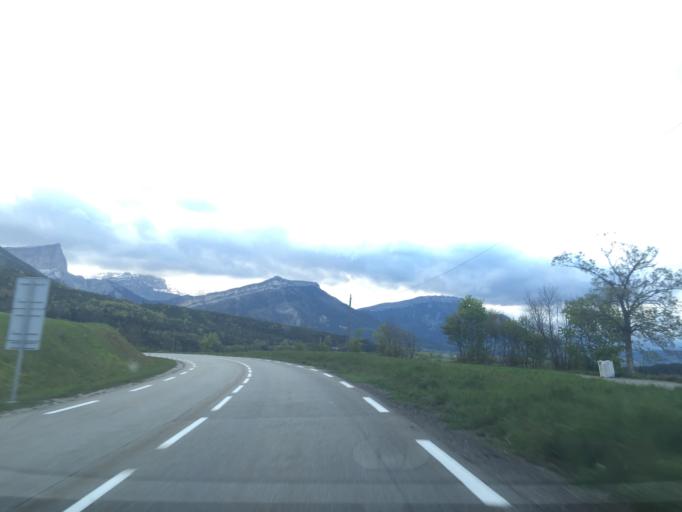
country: FR
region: Rhone-Alpes
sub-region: Departement de l'Isere
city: Mens
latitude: 44.8025
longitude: 5.6372
